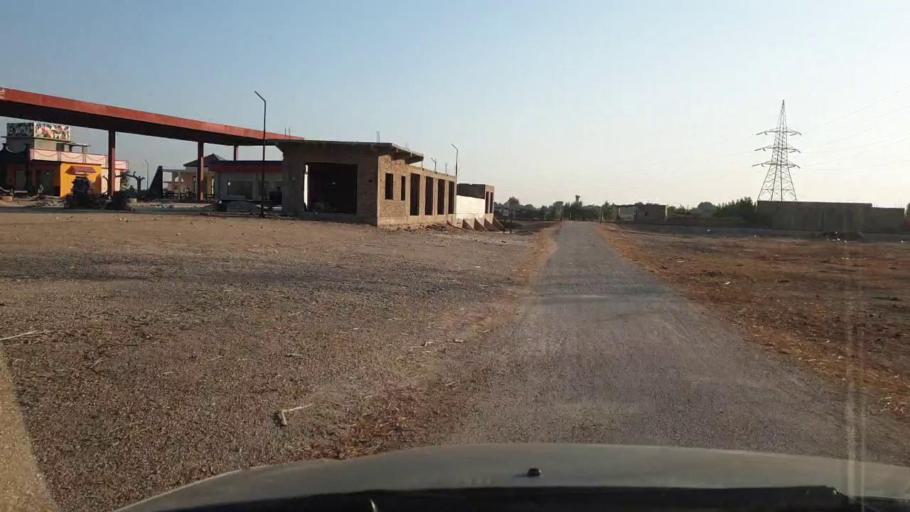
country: PK
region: Sindh
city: Matli
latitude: 25.0453
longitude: 68.6338
